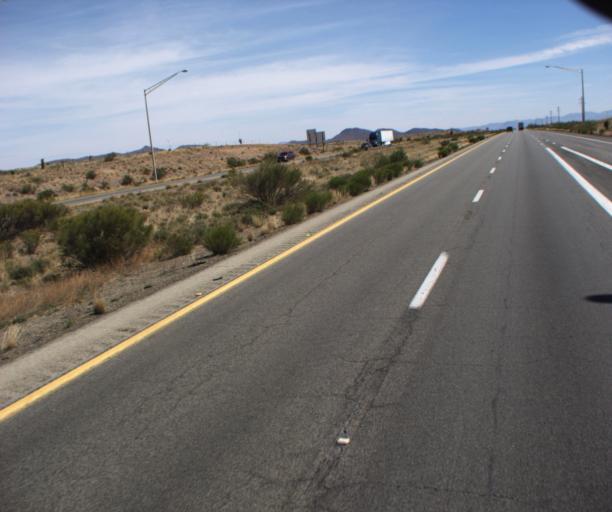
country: US
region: Arizona
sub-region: Cochise County
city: Willcox
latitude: 32.3593
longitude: -109.6759
